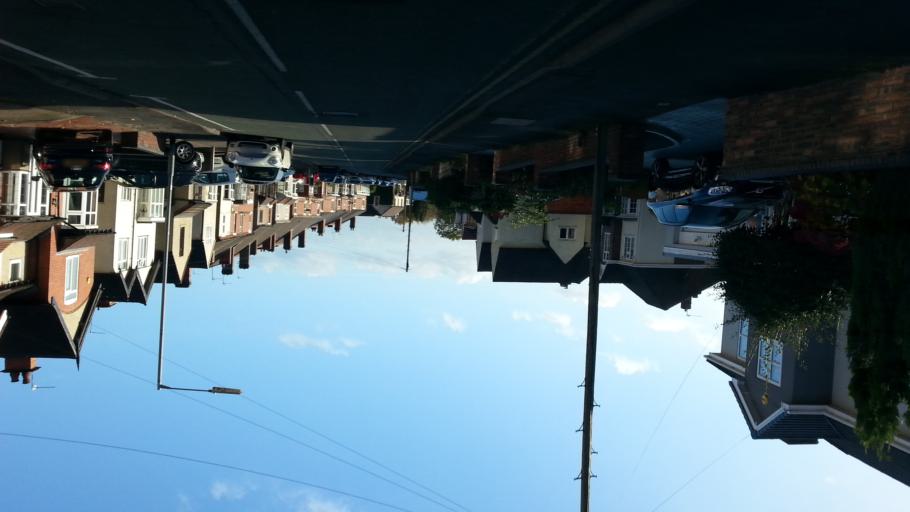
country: GB
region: England
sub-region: Staffordshire
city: Cannock
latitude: 52.6894
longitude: -2.0355
